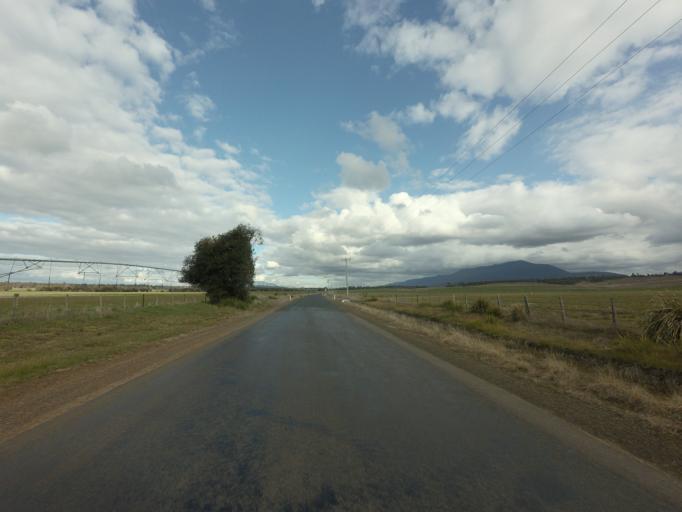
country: AU
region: Tasmania
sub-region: Northern Midlands
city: Longford
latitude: -41.8208
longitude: 147.2025
